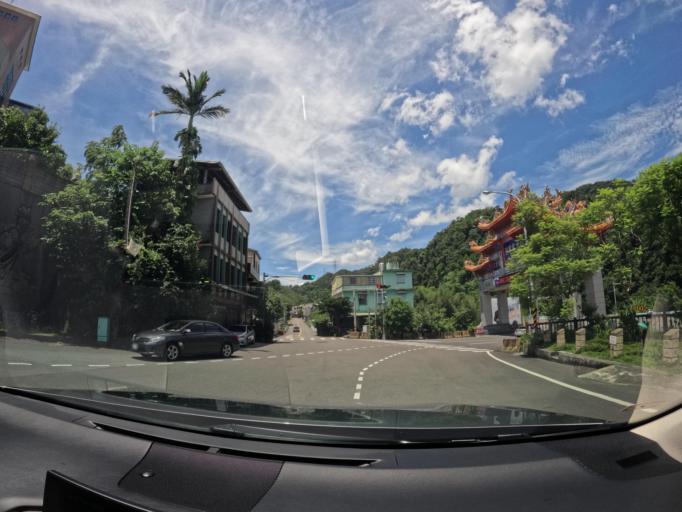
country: TW
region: Taiwan
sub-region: Miaoli
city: Miaoli
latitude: 24.5398
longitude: 120.9199
